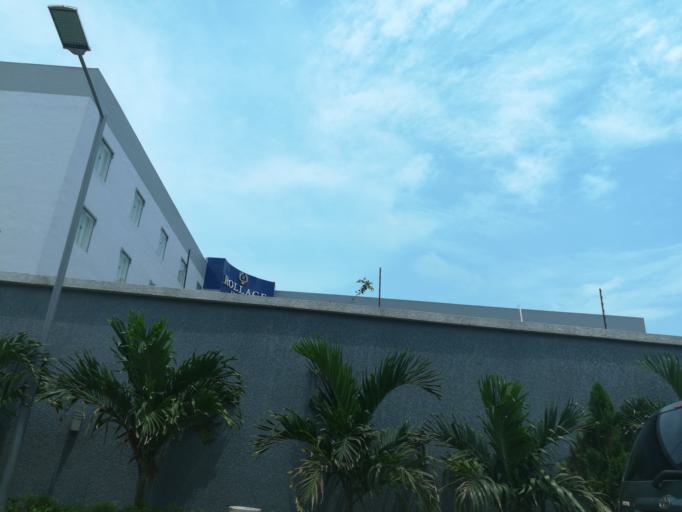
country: NG
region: Lagos
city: Oshodi
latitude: 6.5486
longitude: 3.3280
